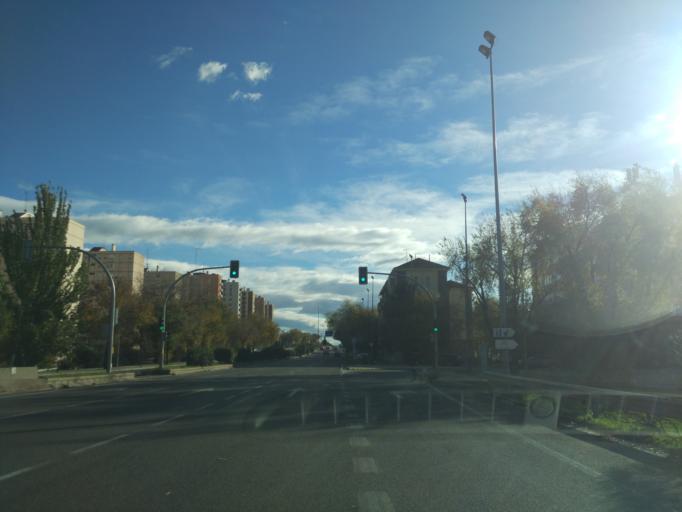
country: ES
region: Madrid
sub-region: Provincia de Madrid
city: Villaverde
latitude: 40.3442
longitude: -3.6930
